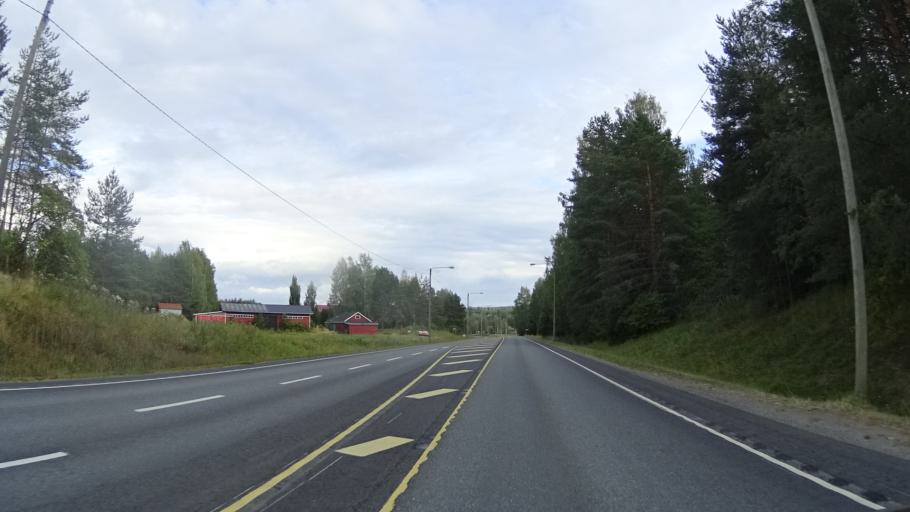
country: FI
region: Haeme
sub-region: Haemeenlinna
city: Parola
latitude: 61.0428
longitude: 24.2446
